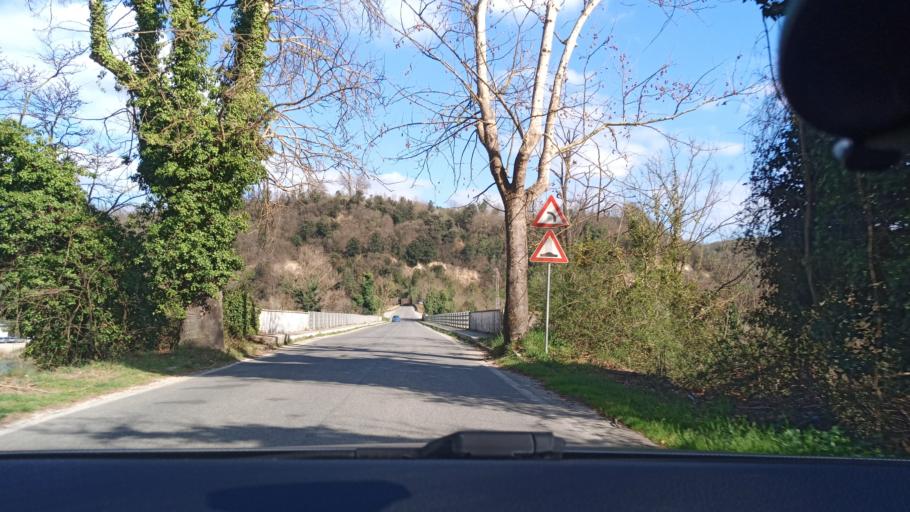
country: IT
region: Latium
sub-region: Citta metropolitana di Roma Capitale
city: Torrita Tiberina
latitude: 42.2355
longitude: 12.6291
